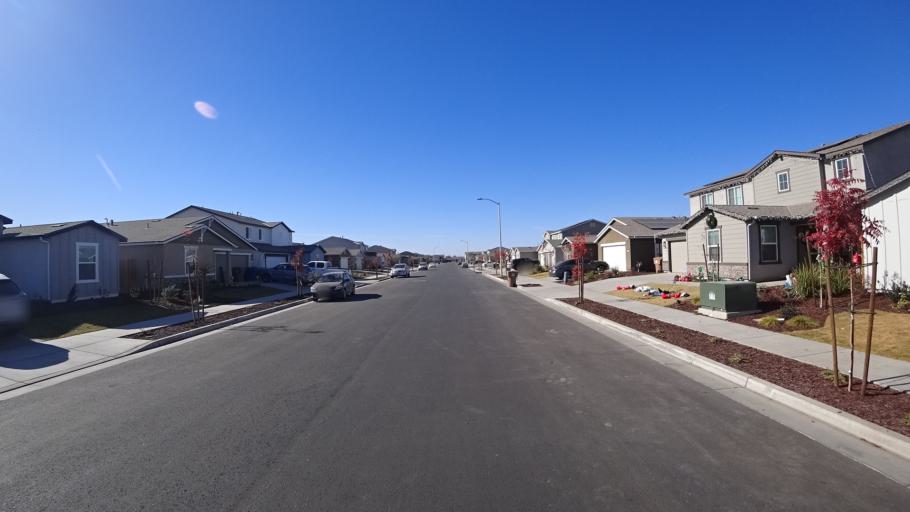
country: US
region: California
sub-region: Kern County
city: Greenfield
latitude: 35.2652
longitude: -119.0681
